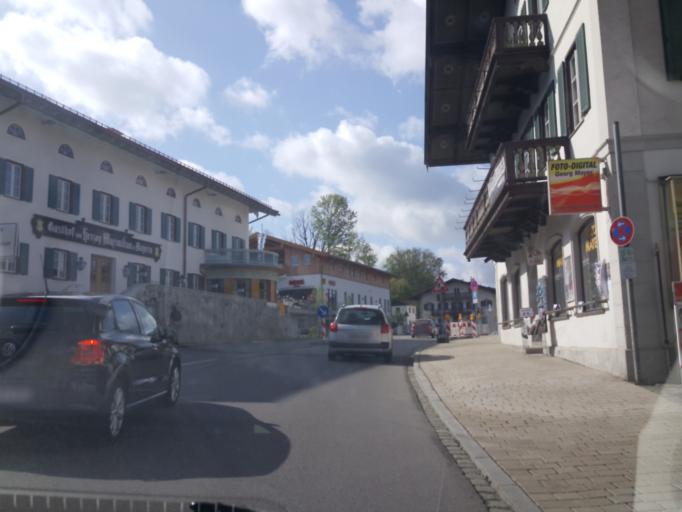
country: DE
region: Bavaria
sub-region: Upper Bavaria
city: Gmund am Tegernsee
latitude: 47.7494
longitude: 11.7391
